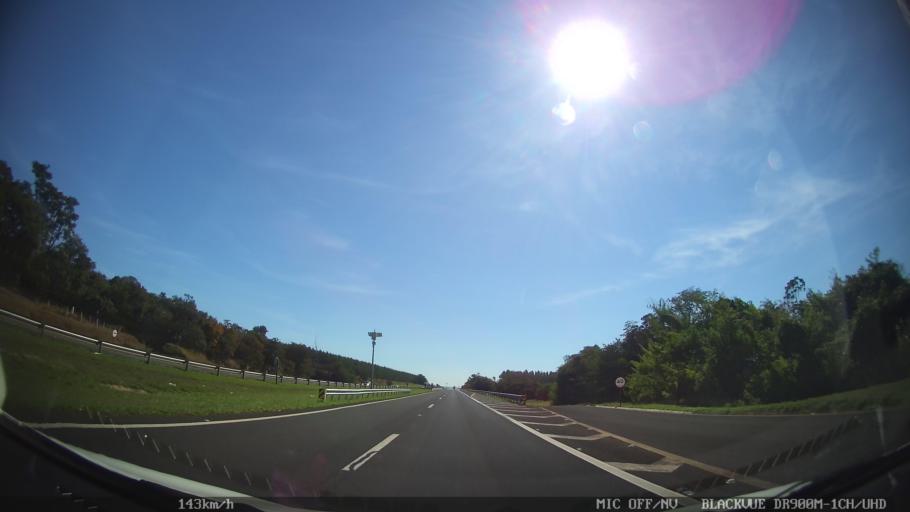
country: BR
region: Sao Paulo
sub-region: Sao Simao
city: Sao Simao
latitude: -21.6117
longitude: -47.6169
